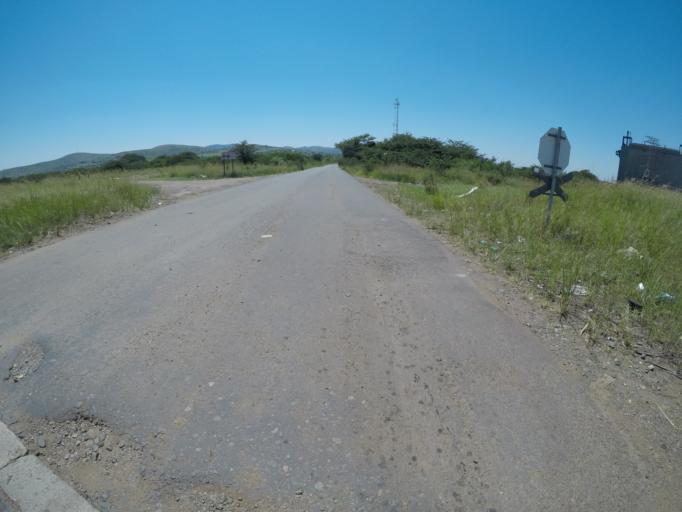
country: ZA
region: KwaZulu-Natal
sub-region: uThungulu District Municipality
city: Empangeni
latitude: -28.7238
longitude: 31.8672
